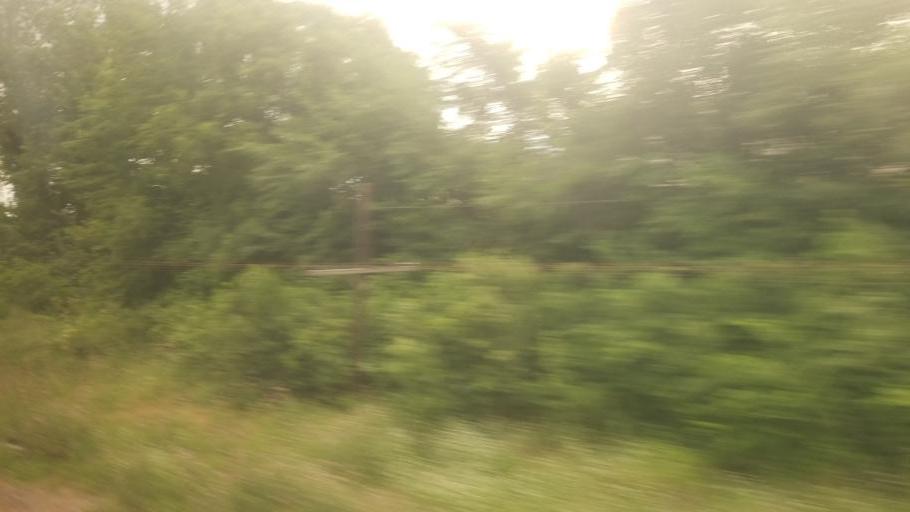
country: US
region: Kansas
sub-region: Shawnee County
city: Topeka
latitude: 38.9730
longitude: -95.6889
